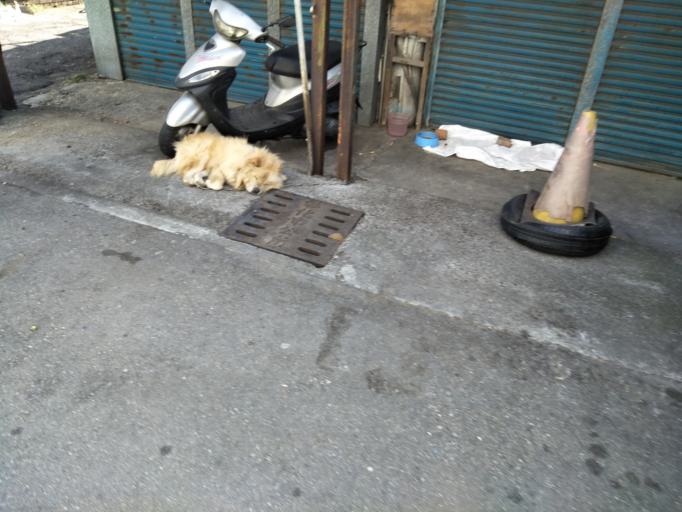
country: TW
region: Taiwan
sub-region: Changhua
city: Chang-hua
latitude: 24.0775
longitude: 120.5388
